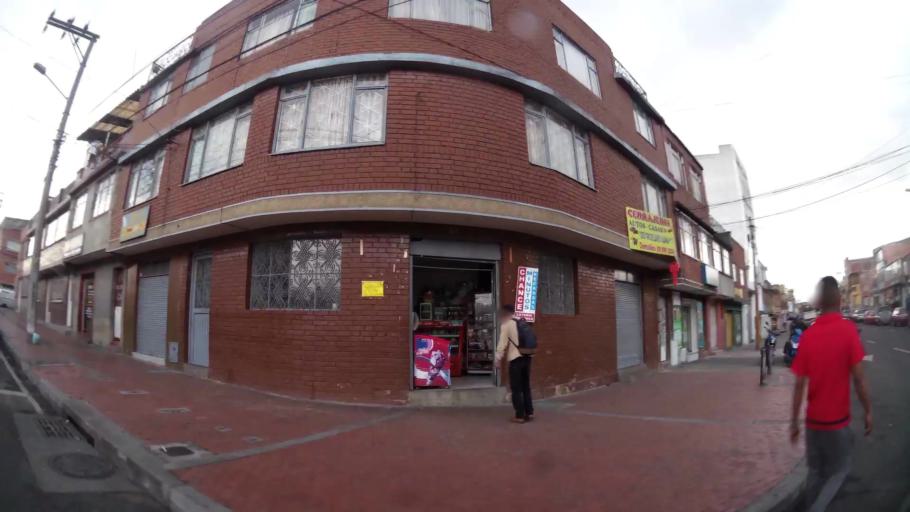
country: CO
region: Bogota D.C.
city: Barrio San Luis
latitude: 4.6757
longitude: -74.0729
